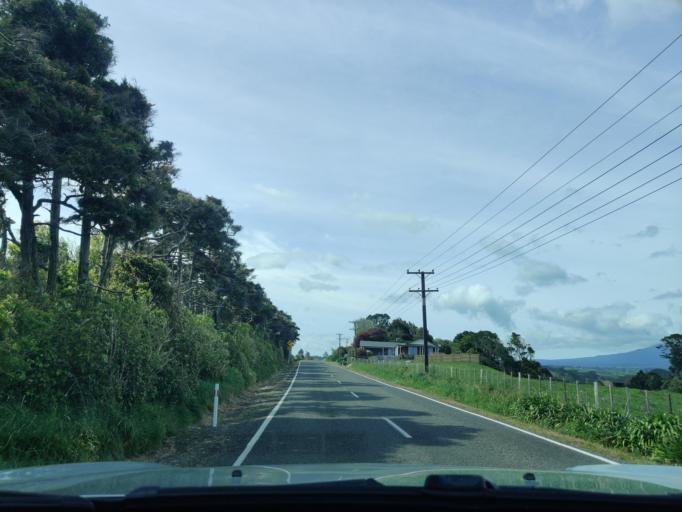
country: NZ
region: Taranaki
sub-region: New Plymouth District
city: New Plymouth
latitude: -39.1085
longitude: 174.1000
